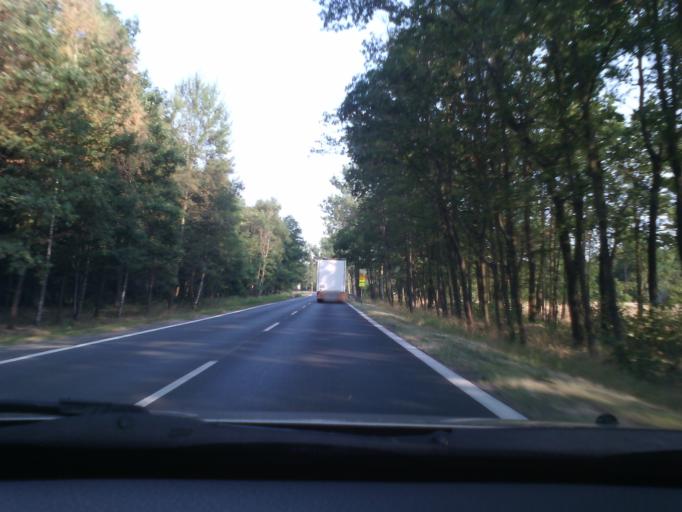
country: PL
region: Lower Silesian Voivodeship
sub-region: Powiat jeleniogorski
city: Janowice Wielkie
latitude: 50.9037
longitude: 15.8654
